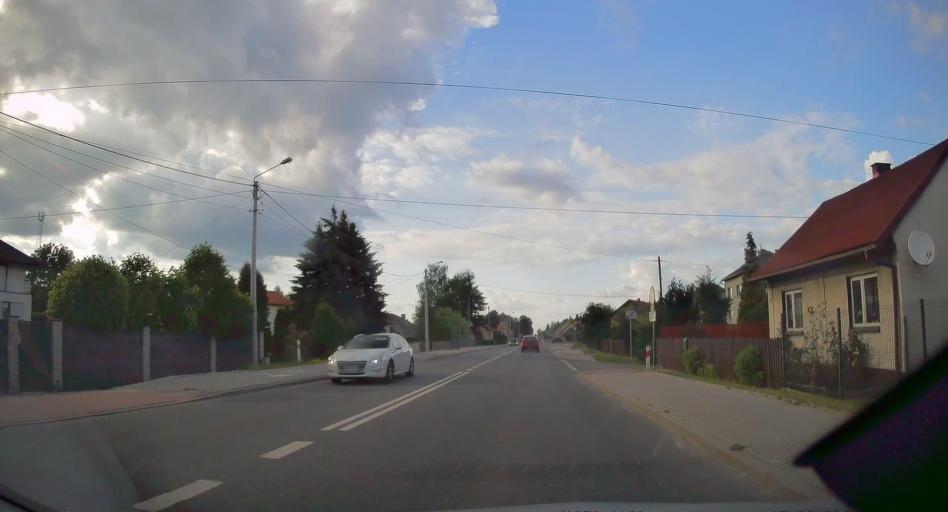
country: PL
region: Lesser Poland Voivodeship
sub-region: Powiat oswiecimski
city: Nowa Wies
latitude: 49.9046
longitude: 19.2170
